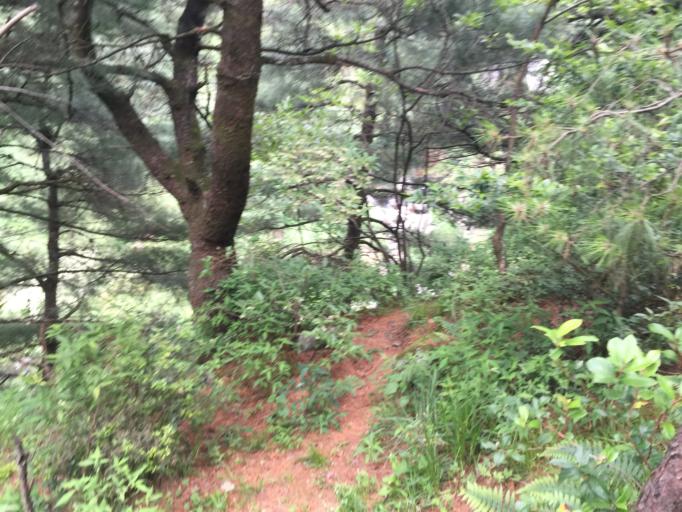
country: CN
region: Yunnan
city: Dali
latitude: 25.6478
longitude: 100.1430
